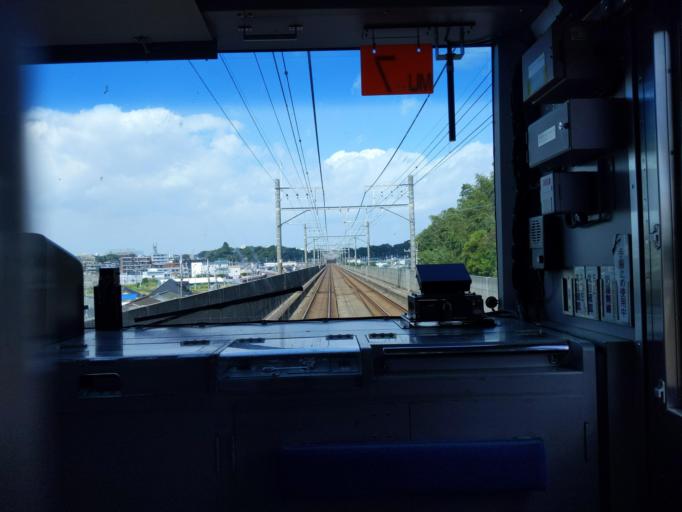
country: JP
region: Chiba
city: Funabashi
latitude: 35.7432
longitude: 139.9594
